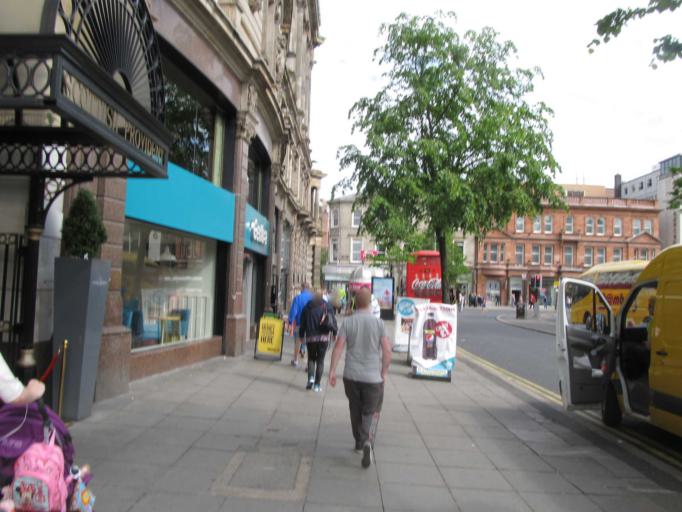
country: GB
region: Northern Ireland
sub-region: City of Belfast
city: Belfast
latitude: 54.5966
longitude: -5.9319
